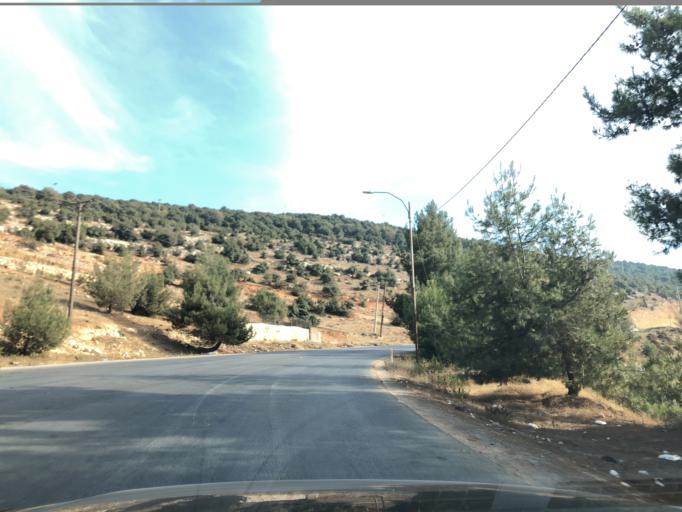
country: JO
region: Irbid
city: `Anjarah
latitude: 32.3117
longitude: 35.7791
